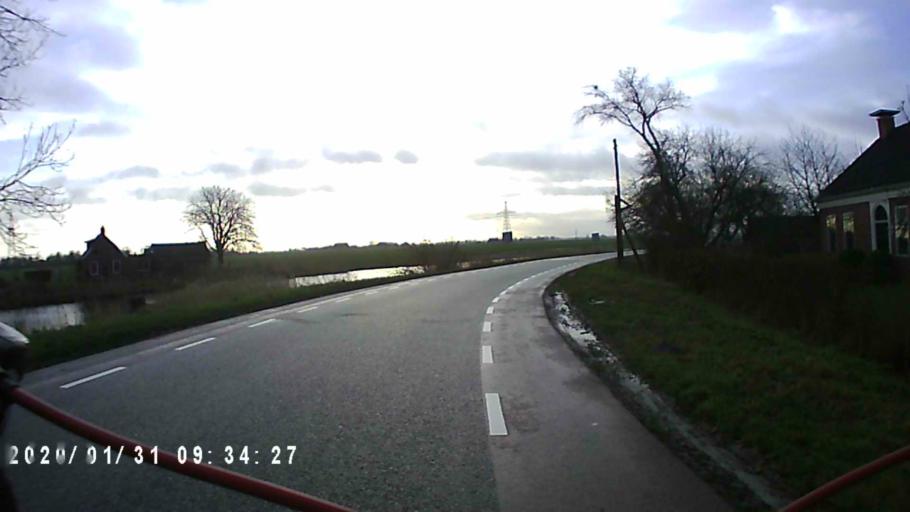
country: NL
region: Groningen
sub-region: Gemeente Winsum
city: Winsum
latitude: 53.3065
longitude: 6.4799
